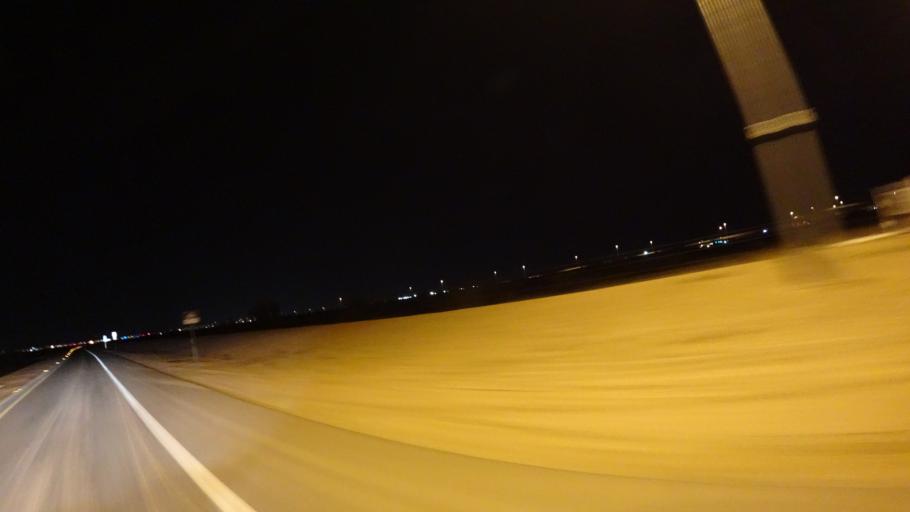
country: US
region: Arizona
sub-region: Maricopa County
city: Queen Creek
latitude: 33.3233
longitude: -111.6531
